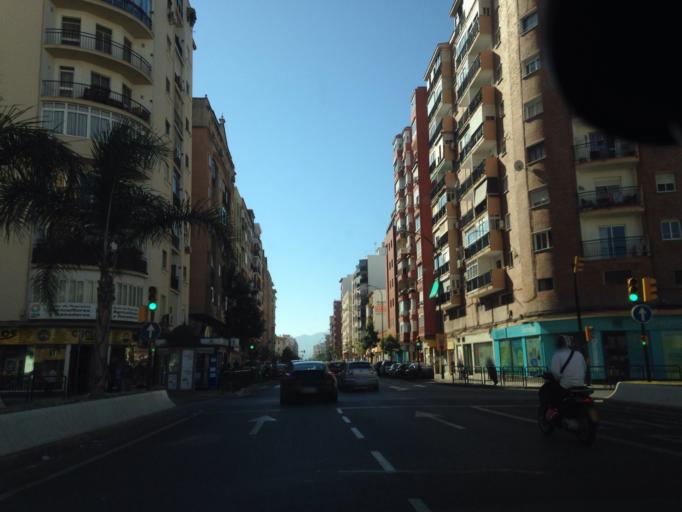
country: ES
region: Andalusia
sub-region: Provincia de Malaga
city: Malaga
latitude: 36.7038
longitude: -4.4406
